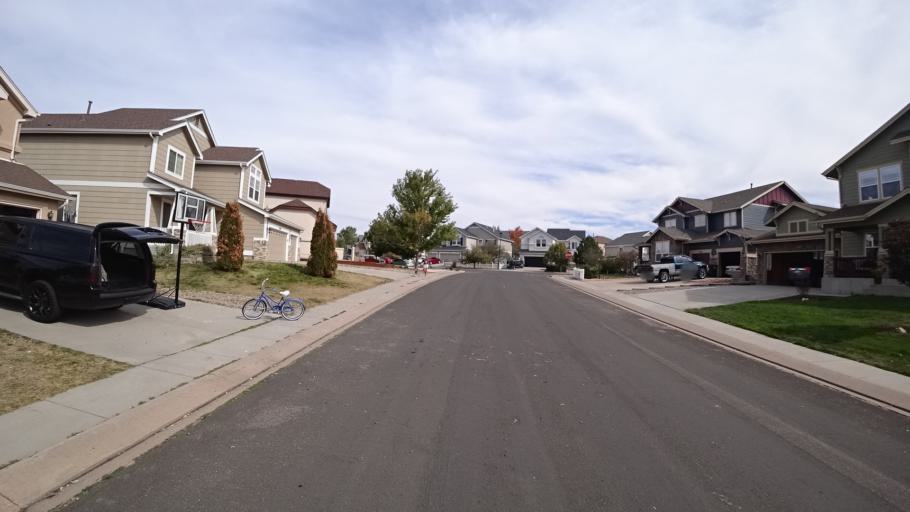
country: US
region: Colorado
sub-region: El Paso County
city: Cimarron Hills
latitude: 38.9112
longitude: -104.6991
